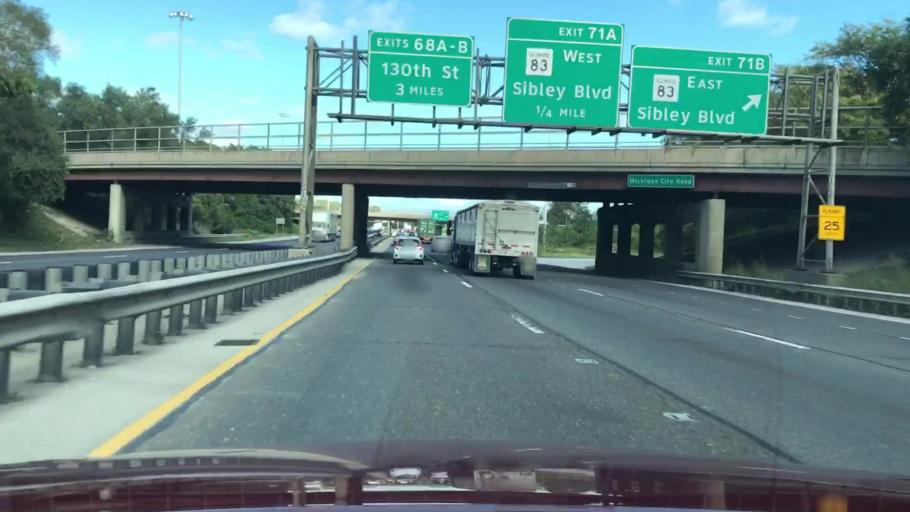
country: US
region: Illinois
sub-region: Cook County
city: Burnham
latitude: 41.6205
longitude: -87.5789
